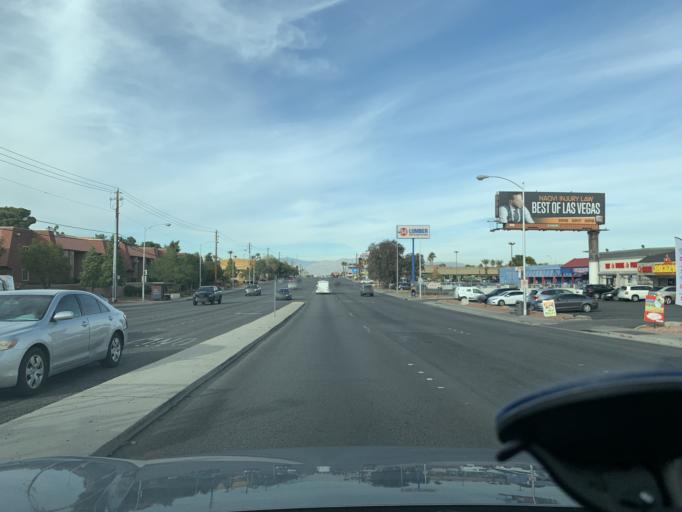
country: US
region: Nevada
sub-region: Clark County
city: Spring Valley
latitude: 36.1101
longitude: -115.2080
